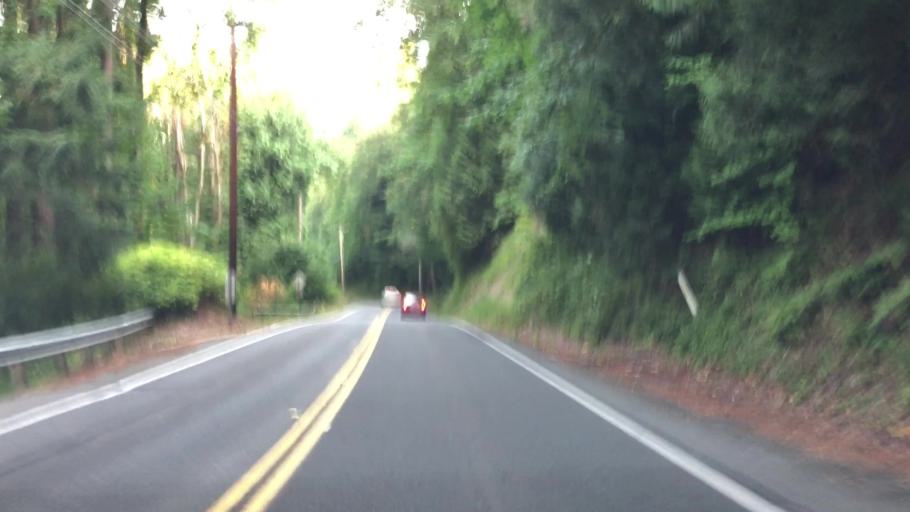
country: US
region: Washington
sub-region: King County
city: Sammamish
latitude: 47.6717
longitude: -122.0705
